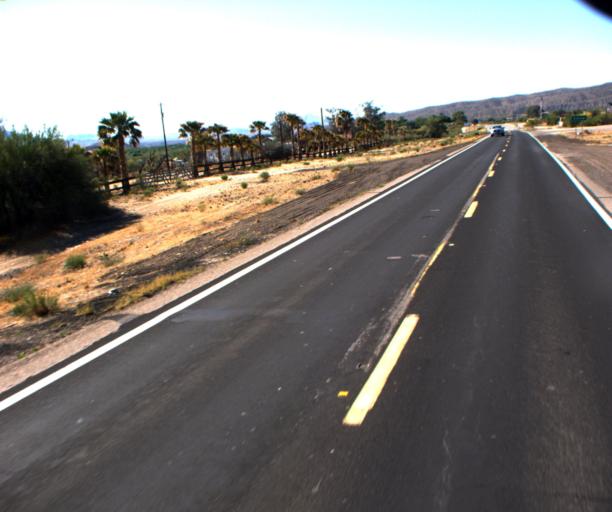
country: US
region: Arizona
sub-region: Yavapai County
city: Bagdad
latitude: 34.7181
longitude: -113.6147
